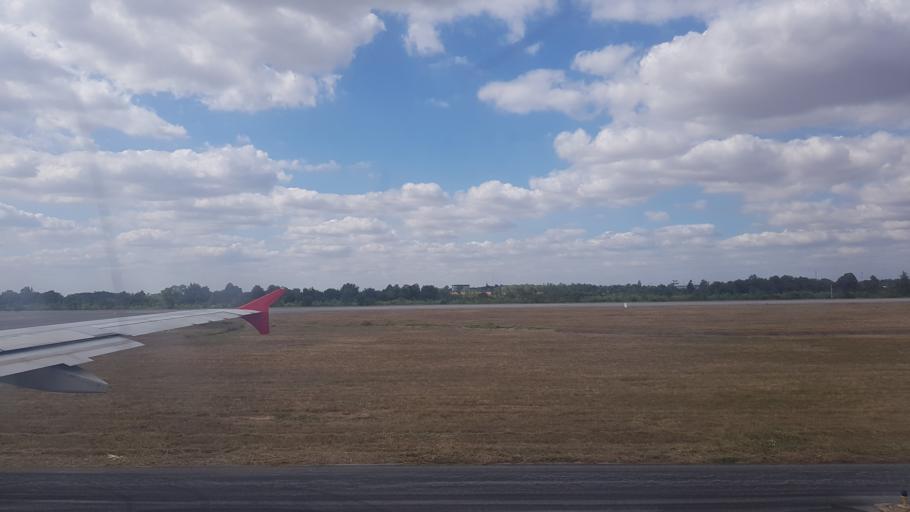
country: TH
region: Khon Kaen
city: Khon Kaen
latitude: 16.4653
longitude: 102.7851
